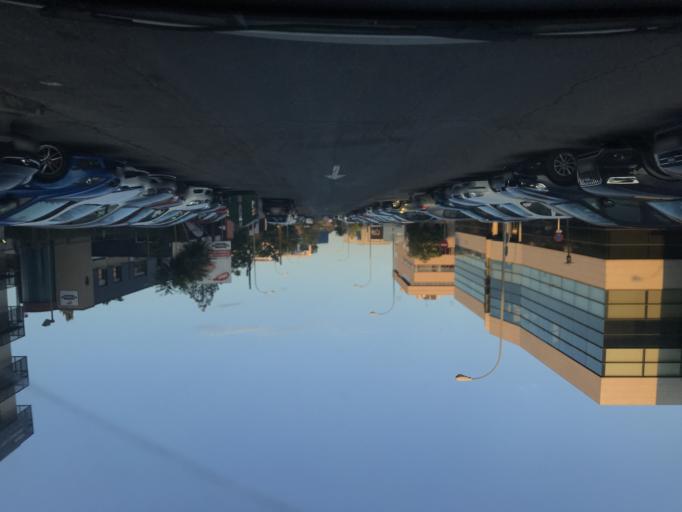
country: ES
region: Madrid
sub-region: Provincia de Madrid
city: Alcobendas
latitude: 40.5338
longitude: -3.6546
